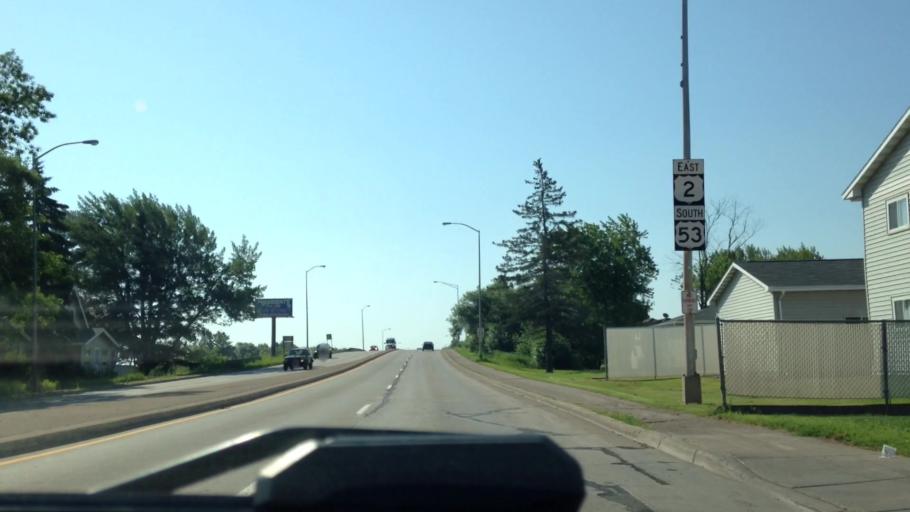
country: US
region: Wisconsin
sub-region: Douglas County
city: Superior
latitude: 46.7051
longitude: -92.0456
